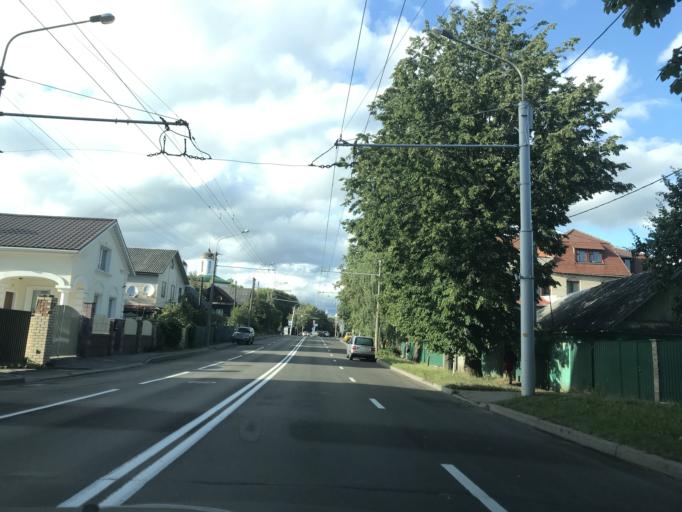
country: BY
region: Minsk
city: Minsk
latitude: 53.9386
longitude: 27.6159
